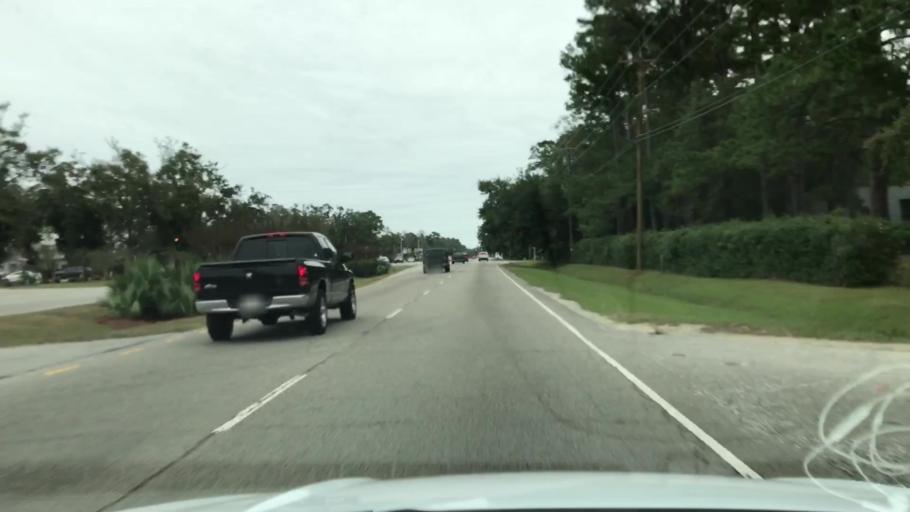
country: US
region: South Carolina
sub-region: Georgetown County
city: Murrells Inlet
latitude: 33.4674
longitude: -79.1075
